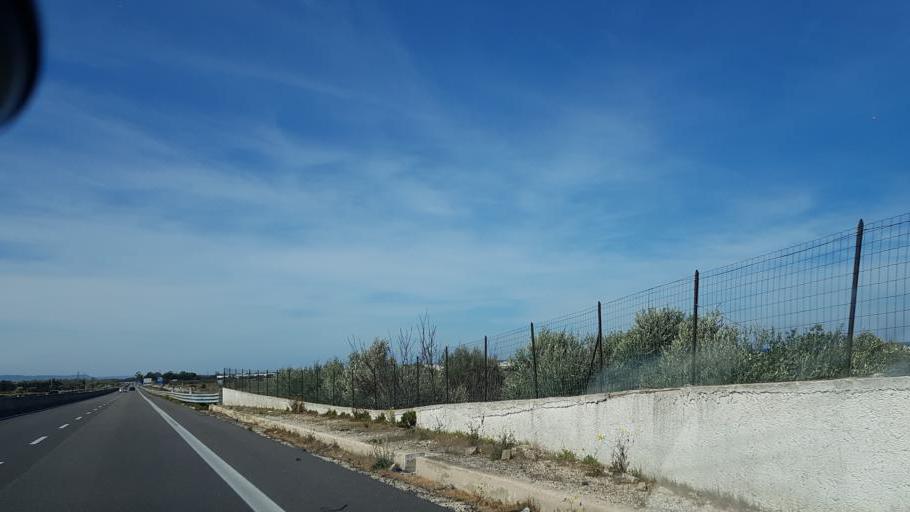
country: IT
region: Apulia
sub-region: Provincia di Brindisi
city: Ostuni
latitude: 40.7809
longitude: 17.5962
